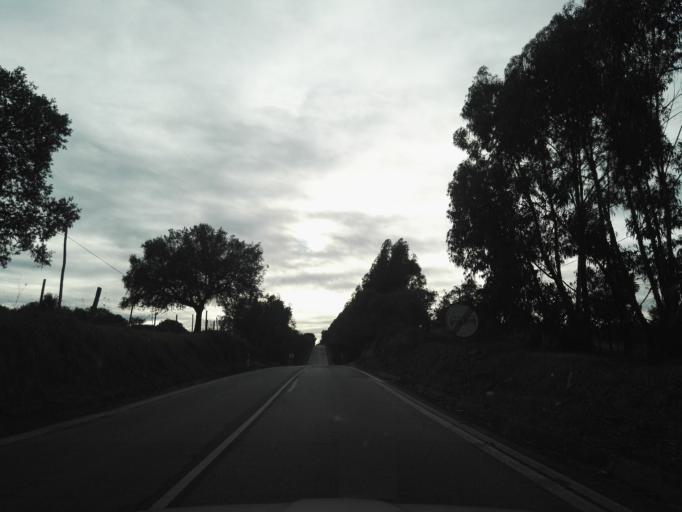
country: PT
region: Evora
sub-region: Redondo
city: Redondo
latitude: 38.6638
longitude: -7.5248
